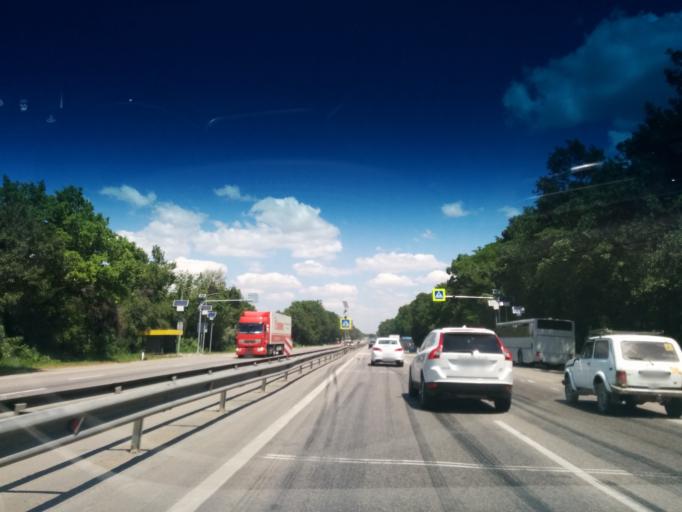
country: RU
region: Rostov
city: Aksay
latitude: 47.3374
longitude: 39.8693
